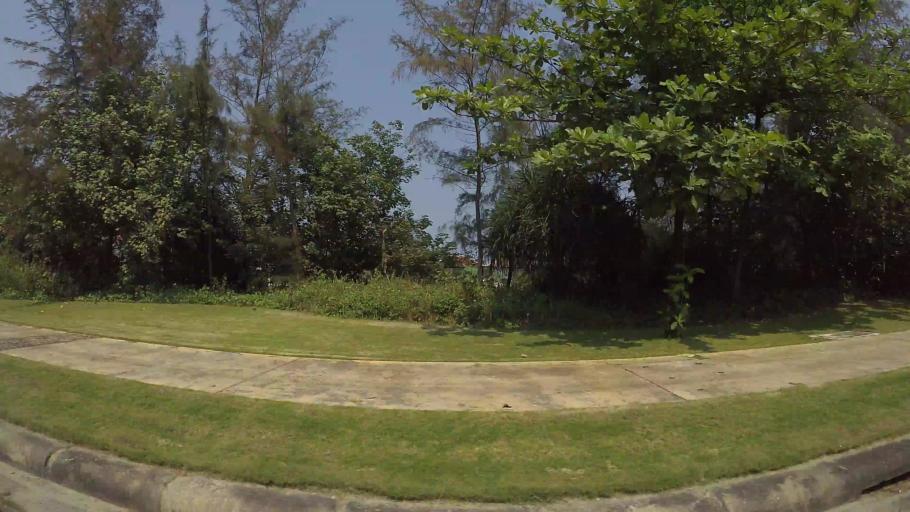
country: VN
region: Da Nang
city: Ngu Hanh Son
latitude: 15.9753
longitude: 108.2792
